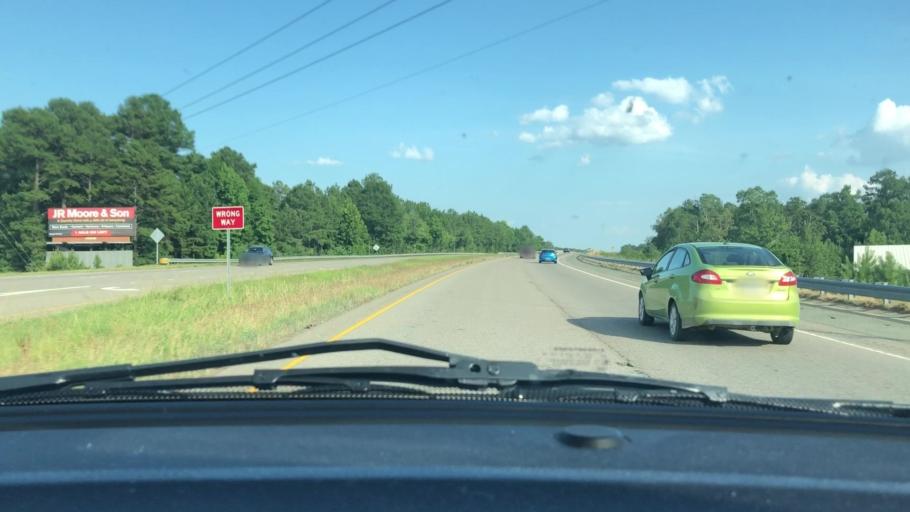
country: US
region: North Carolina
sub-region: Chatham County
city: Farmville
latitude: 35.5679
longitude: -79.3005
